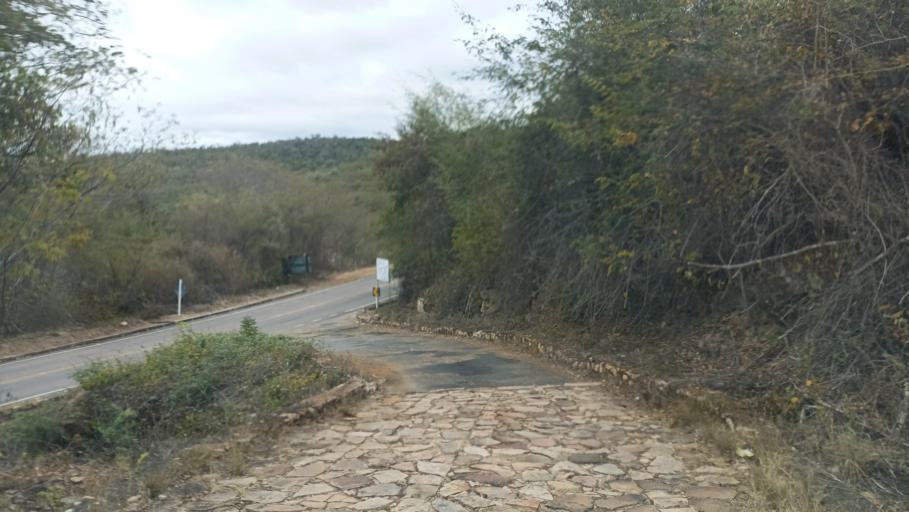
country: BR
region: Bahia
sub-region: Andarai
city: Vera Cruz
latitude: -12.8550
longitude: -41.3114
